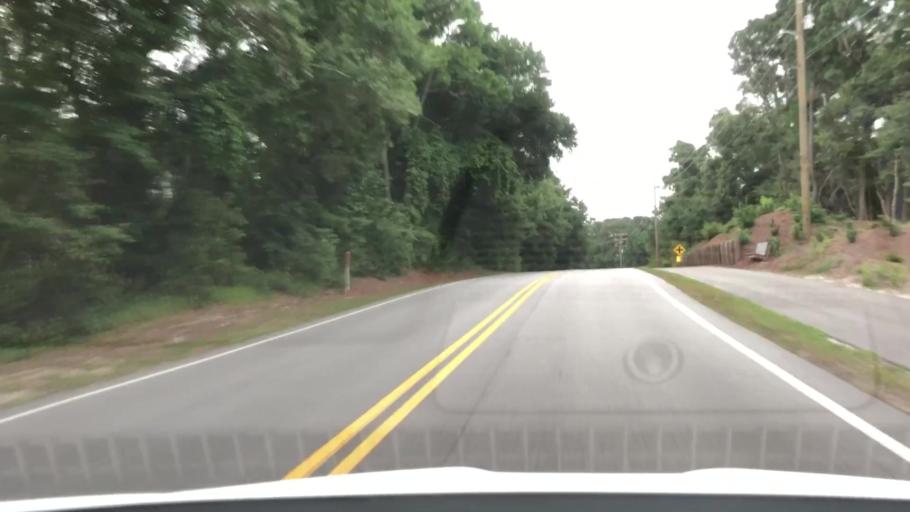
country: US
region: North Carolina
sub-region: Carteret County
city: Cedar Point
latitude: 34.6583
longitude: -77.0759
